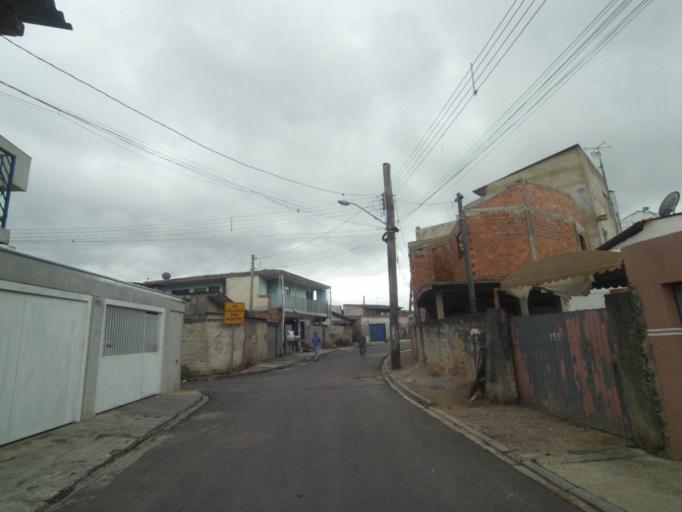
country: BR
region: Parana
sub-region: Curitiba
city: Curitiba
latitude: -25.4849
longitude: -49.3075
